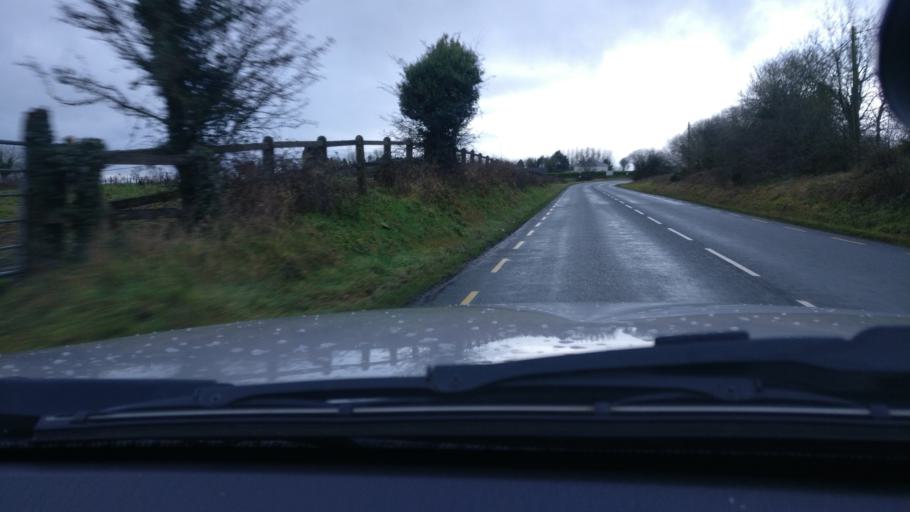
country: IE
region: Leinster
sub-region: An Longfort
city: Granard
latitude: 53.7795
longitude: -7.4700
